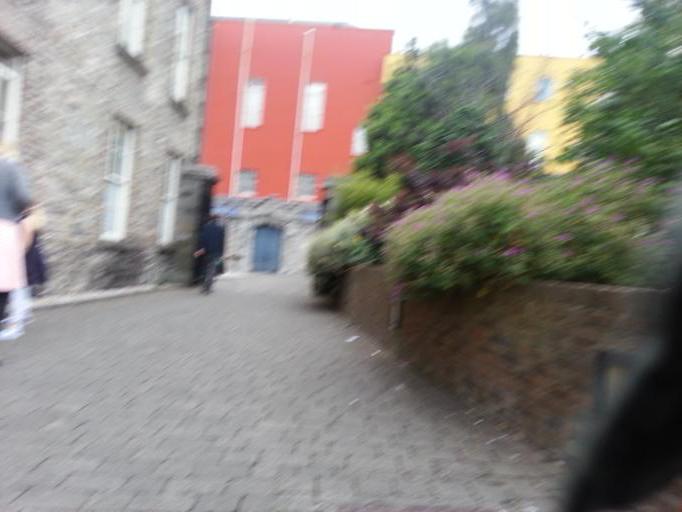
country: IE
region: Leinster
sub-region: Dublin City
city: Dublin
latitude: 53.3423
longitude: -6.2673
